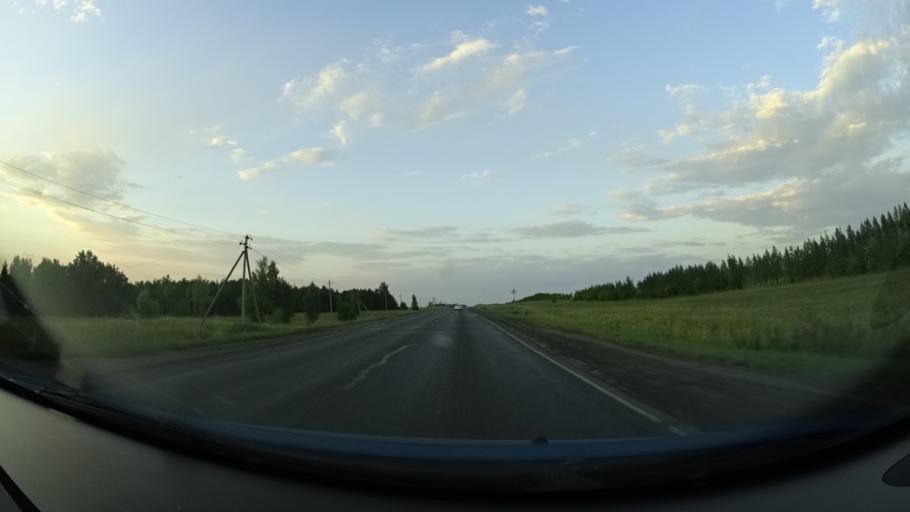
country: RU
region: Orenburg
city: Severnoye
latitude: 54.1993
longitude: 52.6869
